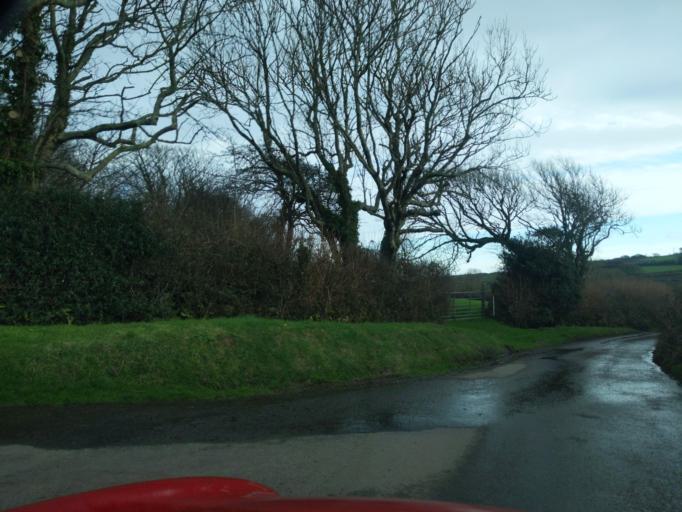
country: GB
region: England
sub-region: Devon
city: Salcombe
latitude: 50.2608
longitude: -3.6825
